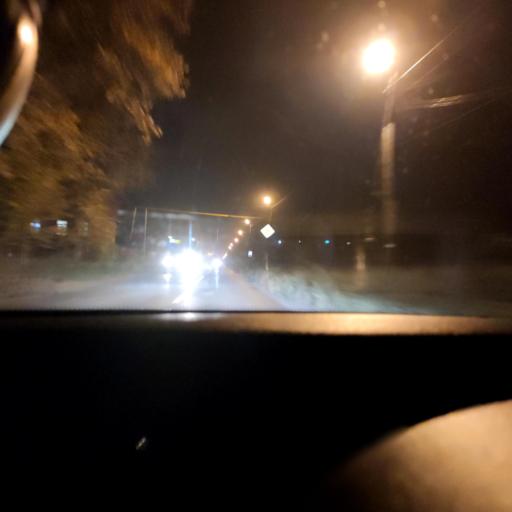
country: RU
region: Samara
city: Petra-Dubrava
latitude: 53.2544
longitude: 50.3249
